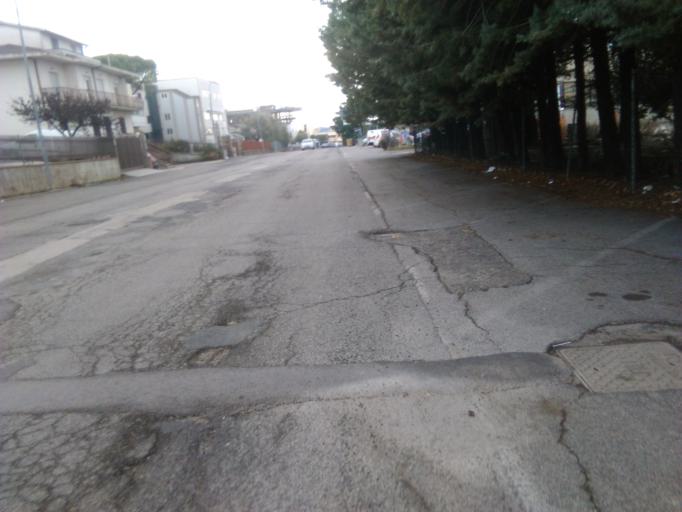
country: IT
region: Umbria
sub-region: Provincia di Perugia
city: Perugia
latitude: 43.0942
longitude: 12.3631
